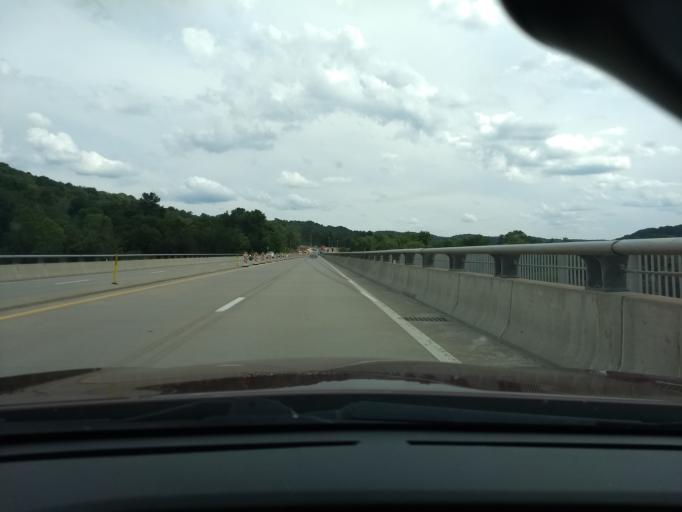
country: US
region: Pennsylvania
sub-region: Armstrong County
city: Freeport
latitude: 40.6683
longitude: -79.6921
